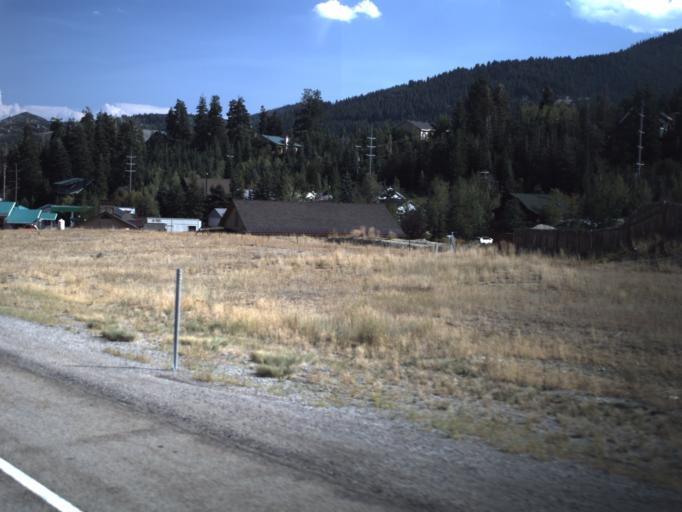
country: US
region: Utah
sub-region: Summit County
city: Summit Park
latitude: 40.7529
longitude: -111.6174
